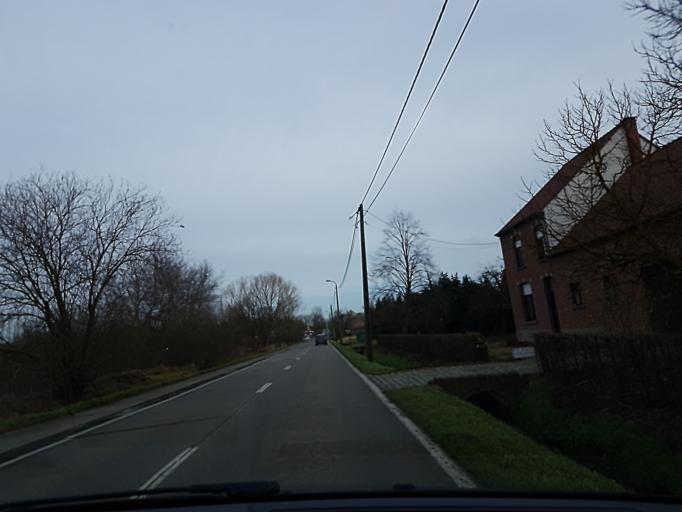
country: BE
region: Flanders
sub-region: Provincie Antwerpen
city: Putte
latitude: 51.0371
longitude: 4.6171
